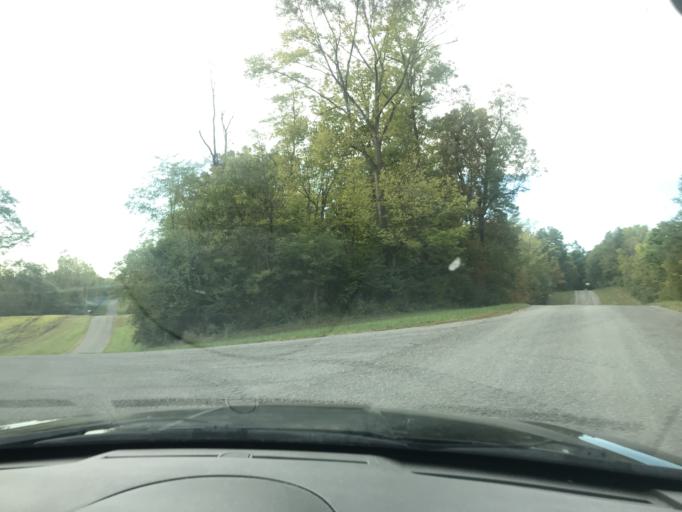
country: US
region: Ohio
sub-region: Logan County
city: West Liberty
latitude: 40.2241
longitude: -83.6610
